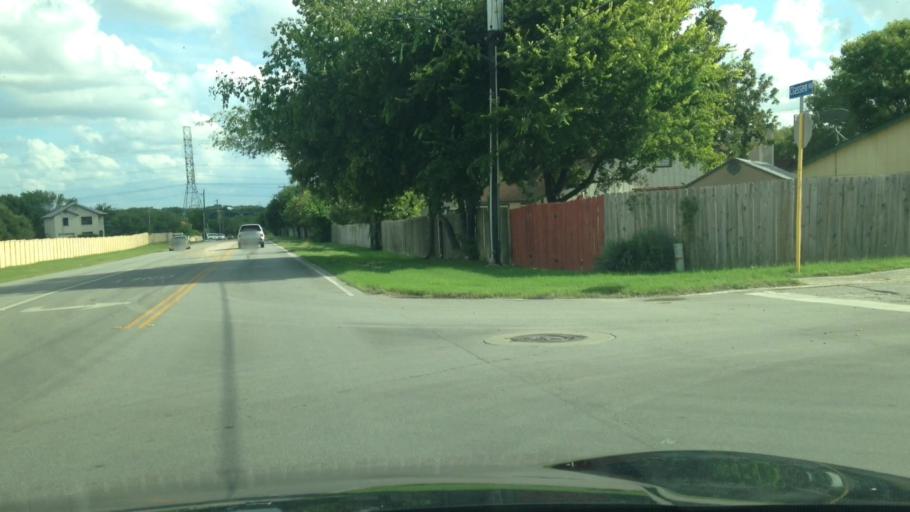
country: US
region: Texas
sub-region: Bexar County
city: Live Oak
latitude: 29.5854
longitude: -98.4057
